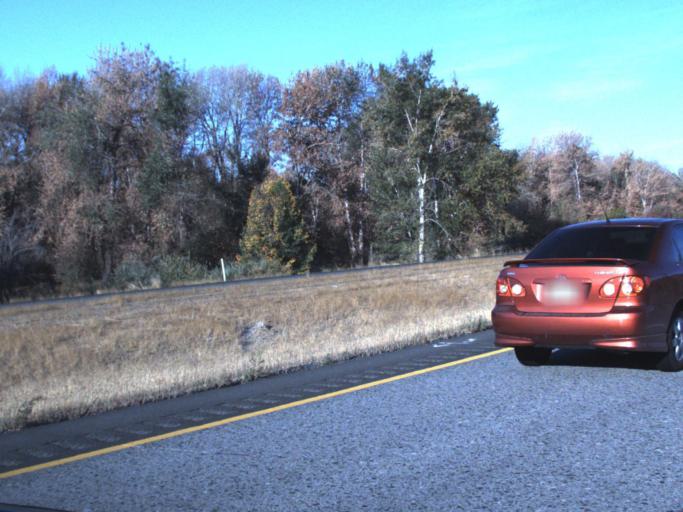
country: US
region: Washington
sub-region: Yakima County
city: Wapato
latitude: 46.4491
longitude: -120.3562
